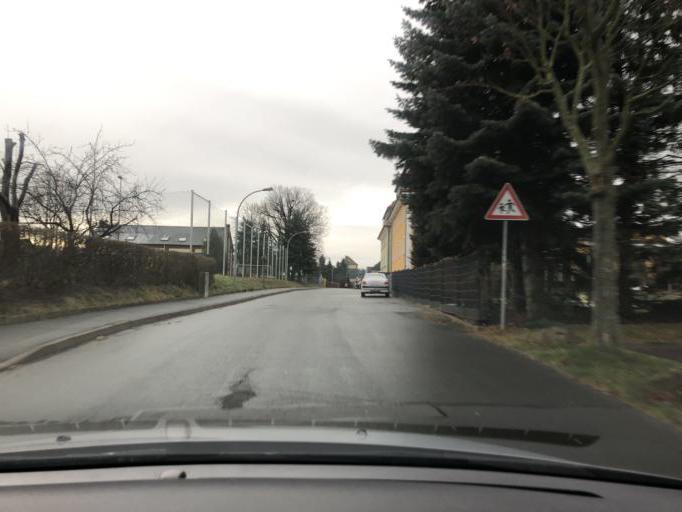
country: DE
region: Saxony
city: Limbach-Oberfrohna
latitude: 50.8539
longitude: 12.7281
